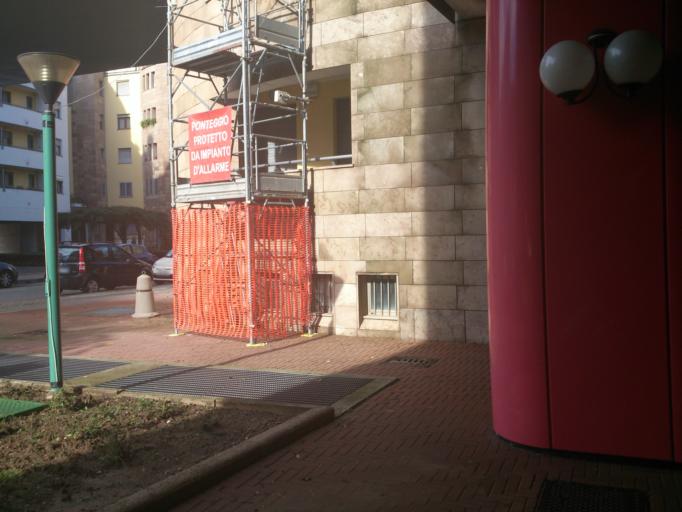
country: IT
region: Lombardy
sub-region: Citta metropolitana di Milano
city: San Donato Milanese
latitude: 45.4185
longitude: 9.2577
